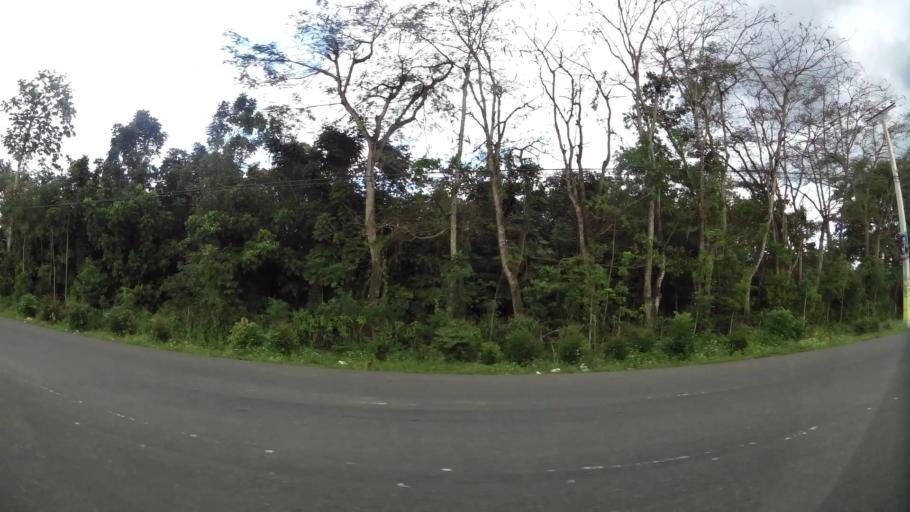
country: DO
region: Monsenor Nouel
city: Bonao
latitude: 18.9557
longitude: -70.4039
